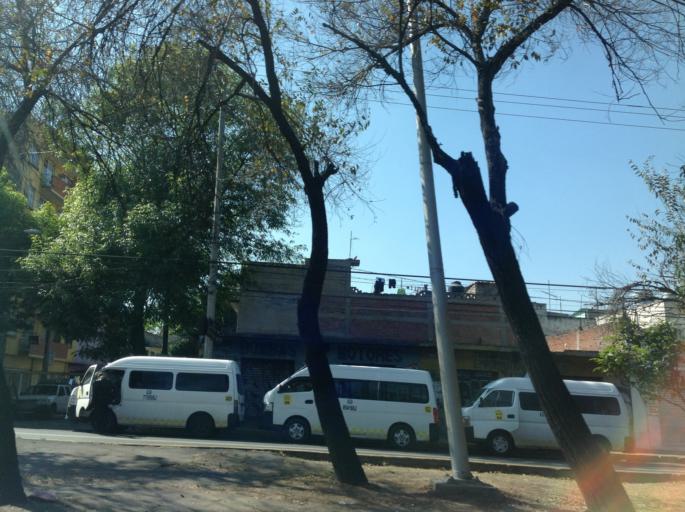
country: MX
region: Mexico City
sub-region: Iztacalco
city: Iztacalco
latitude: 19.4165
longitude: -99.0912
